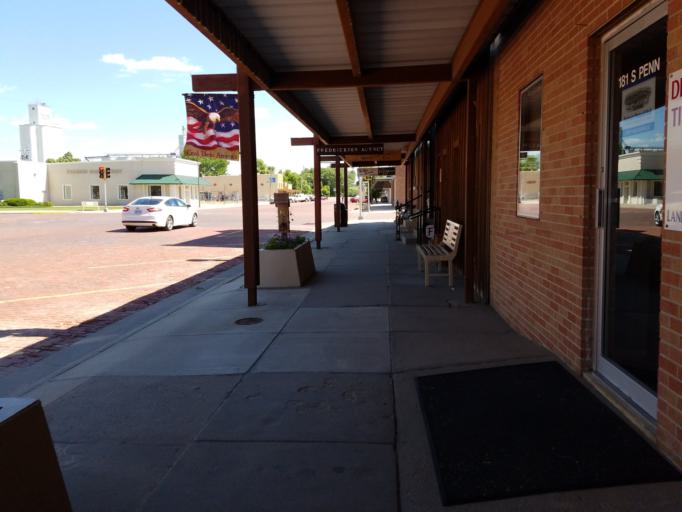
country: US
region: Kansas
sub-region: Decatur County
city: Oberlin
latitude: 39.8195
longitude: -100.5292
